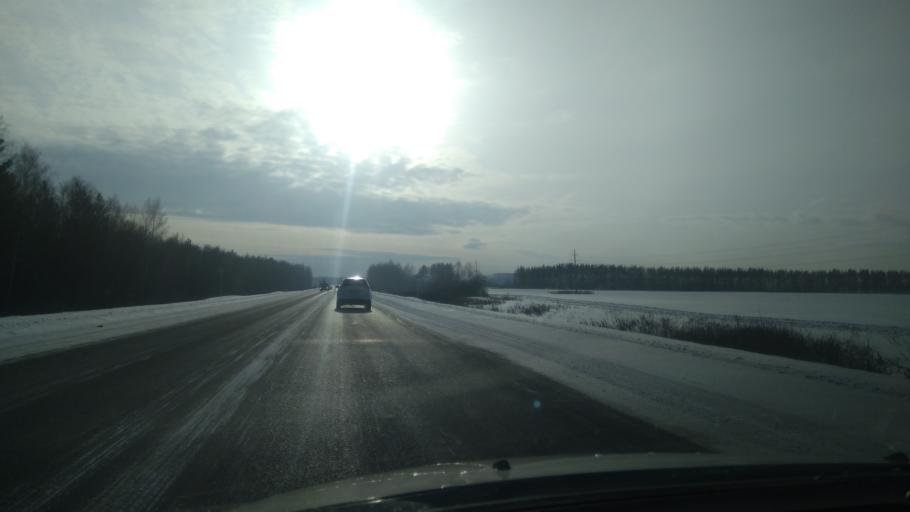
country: RU
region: Sverdlovsk
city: Bogdanovich
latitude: 56.8360
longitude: 62.0513
